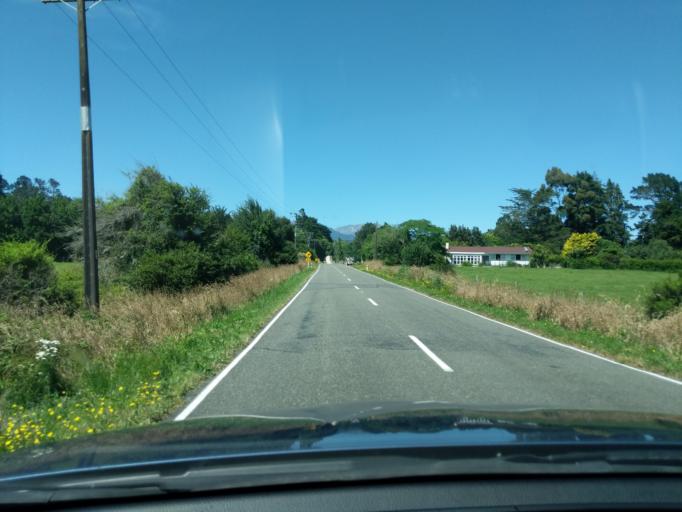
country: NZ
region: Tasman
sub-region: Tasman District
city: Takaka
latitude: -40.7270
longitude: 172.6372
